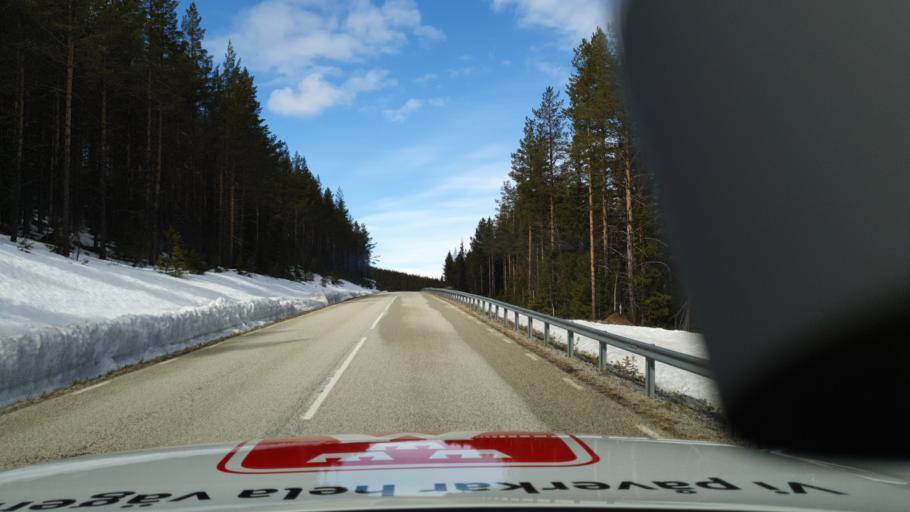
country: SE
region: Jaemtland
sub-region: Are Kommun
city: Are
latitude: 62.8310
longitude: 13.2027
